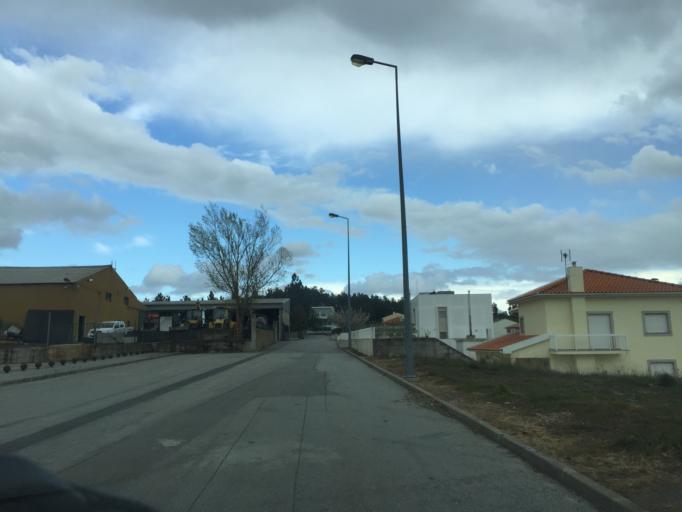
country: PT
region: Braganca
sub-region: Mogadouro
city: Mogadouro
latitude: 41.3429
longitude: -6.7022
